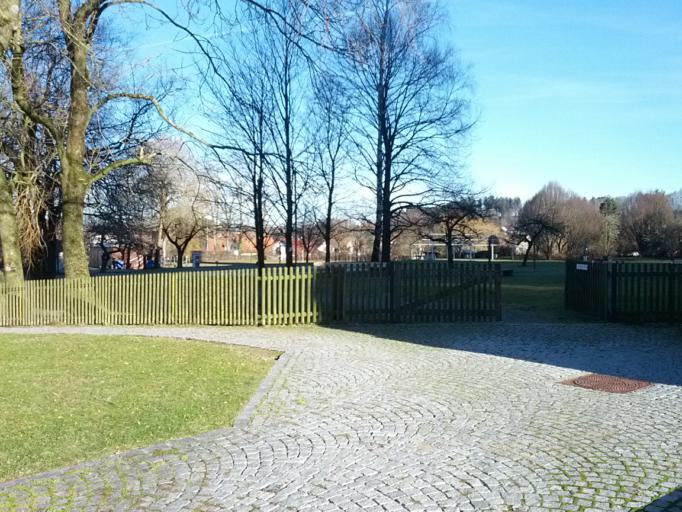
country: DE
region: Baden-Wuerttemberg
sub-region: Tuebingen Region
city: Rot an der Rot
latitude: 48.0150
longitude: 10.0295
